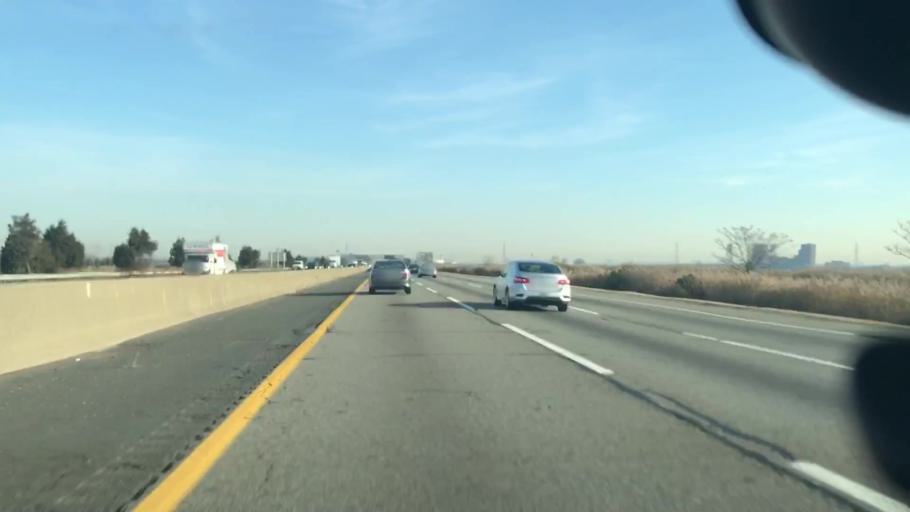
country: US
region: New Jersey
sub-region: Bergen County
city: North Arlington
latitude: 40.7696
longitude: -74.1070
